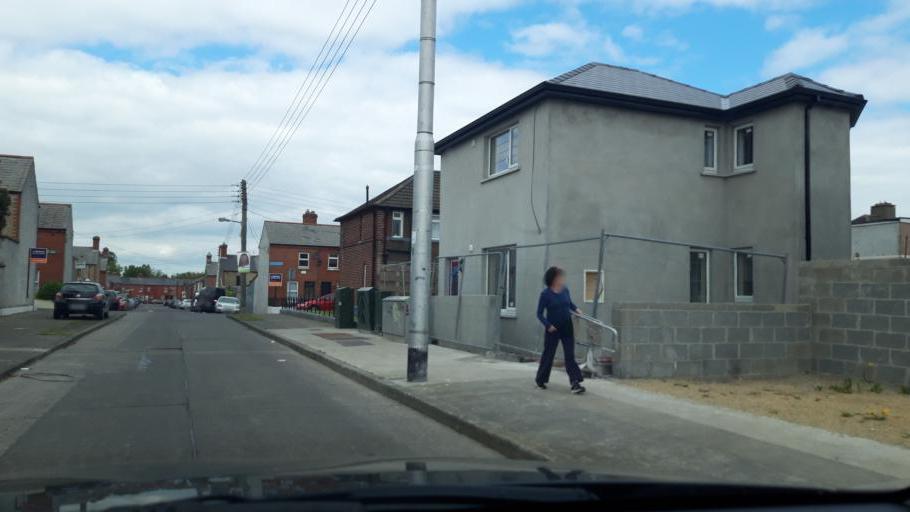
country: IE
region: Leinster
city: Crumlin
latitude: 53.3357
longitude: -6.3299
